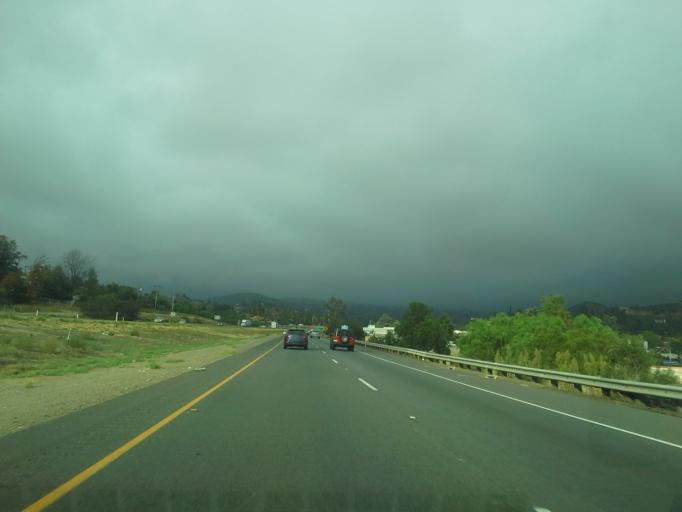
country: US
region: California
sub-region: San Diego County
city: Crest
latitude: 32.8479
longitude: -116.8731
